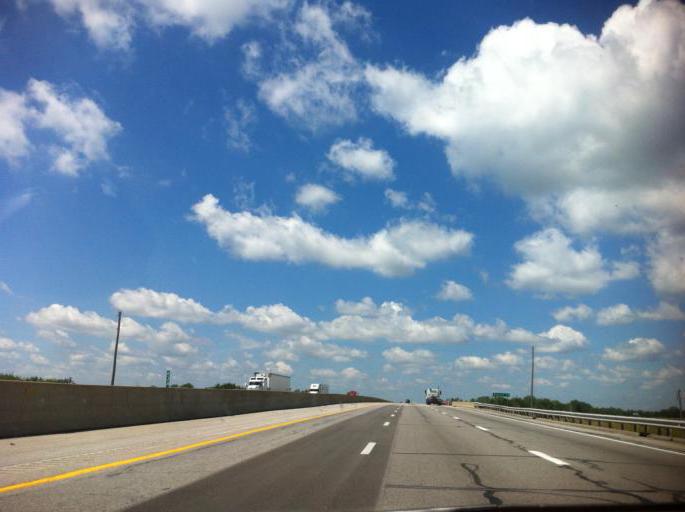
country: US
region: Ohio
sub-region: Ottawa County
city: Elmore
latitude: 41.4477
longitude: -83.2584
